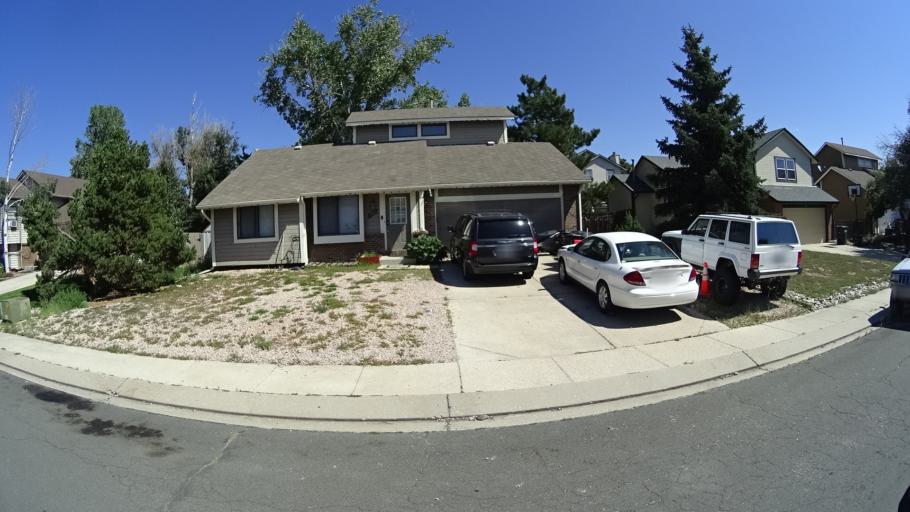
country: US
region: Colorado
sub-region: El Paso County
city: Black Forest
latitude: 38.9393
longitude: -104.7641
